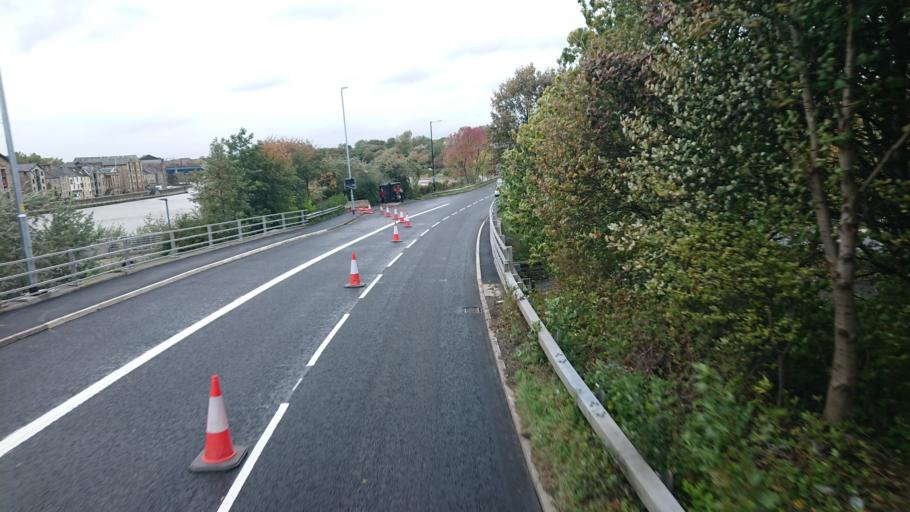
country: GB
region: England
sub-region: Lancashire
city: Lancaster
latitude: 54.0528
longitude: -2.8016
